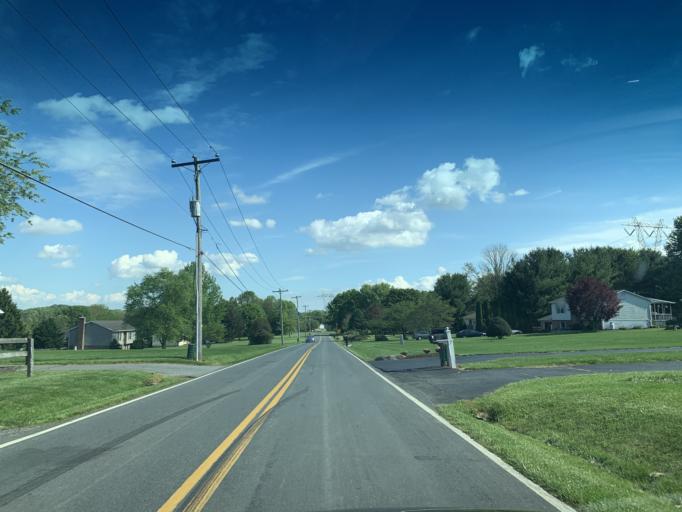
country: US
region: Maryland
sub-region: Cecil County
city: Rising Sun
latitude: 39.6966
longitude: -76.1409
